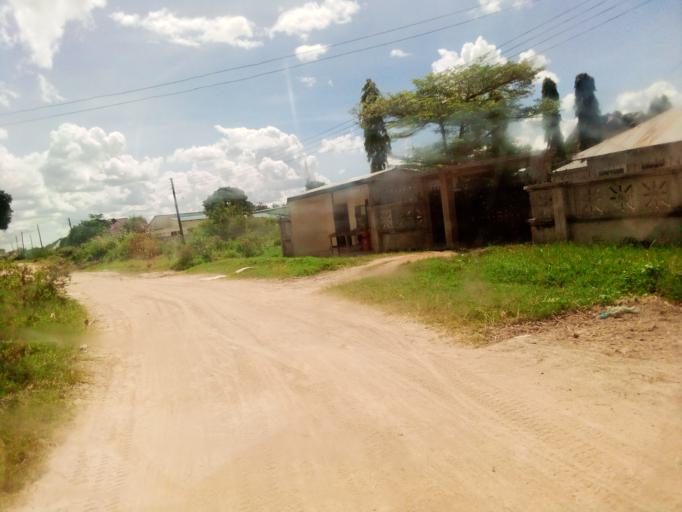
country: TZ
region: Dodoma
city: Kisasa
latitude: -6.1640
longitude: 35.7671
